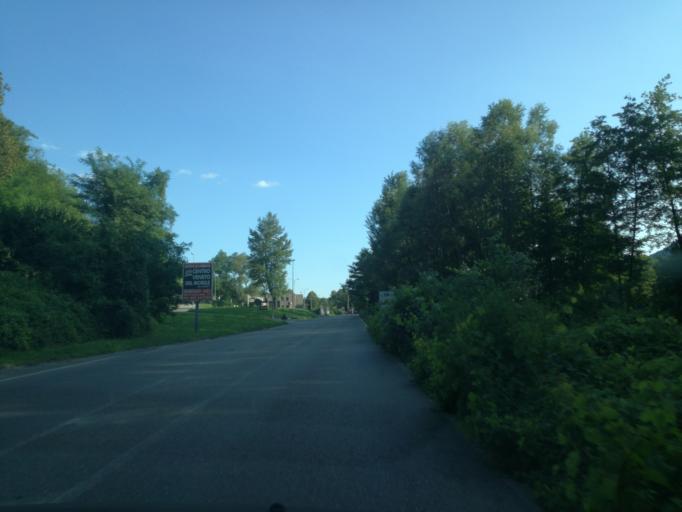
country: IT
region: Lombardy
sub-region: Provincia di Lecco
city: Monte Marenzo
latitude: 45.7741
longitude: 9.4434
